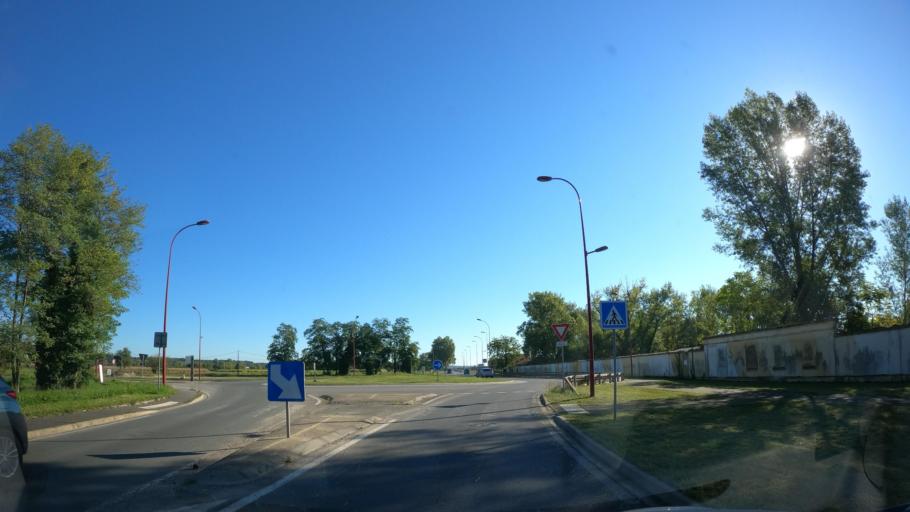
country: FR
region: Aquitaine
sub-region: Departement de la Dordogne
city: Cours-de-Pile
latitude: 44.8471
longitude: 0.5201
